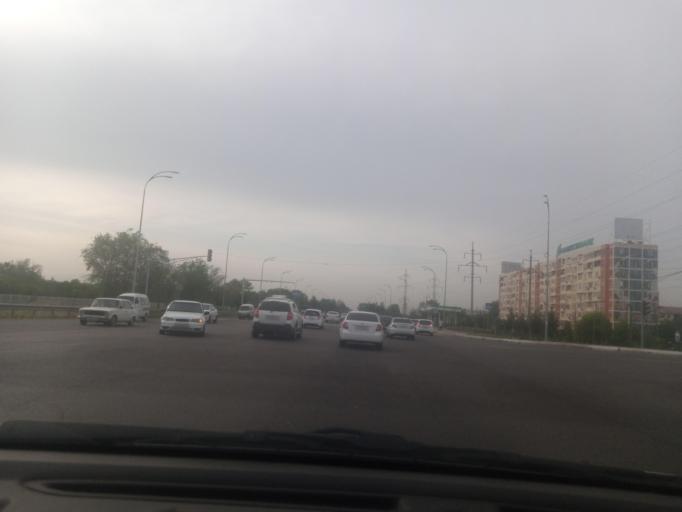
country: UZ
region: Toshkent Shahri
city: Bektemir
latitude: 41.2580
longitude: 69.3790
